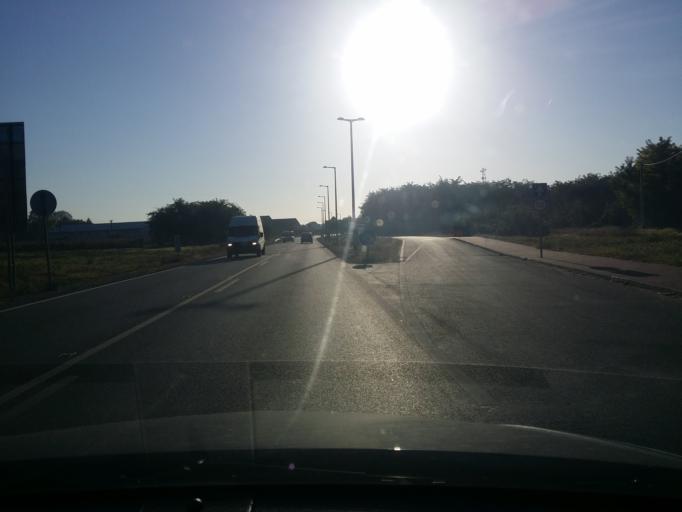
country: HU
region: Bacs-Kiskun
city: Kecskemet
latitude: 46.9064
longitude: 19.7413
